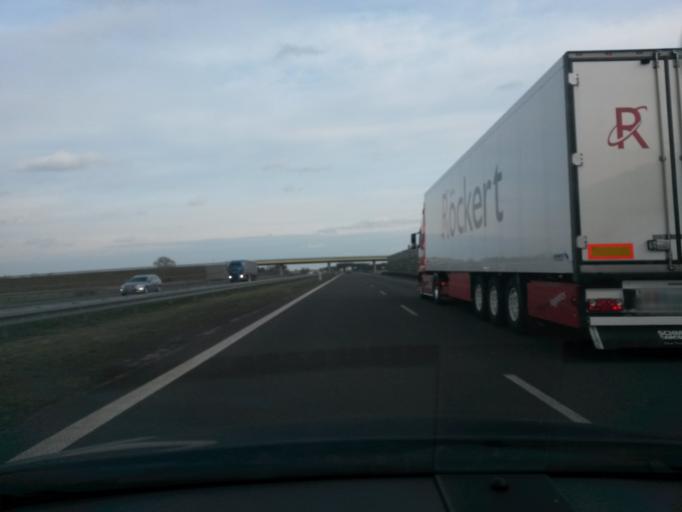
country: PL
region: Greater Poland Voivodeship
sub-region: Powiat kolski
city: Dabie
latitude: 52.1077
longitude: 18.7484
